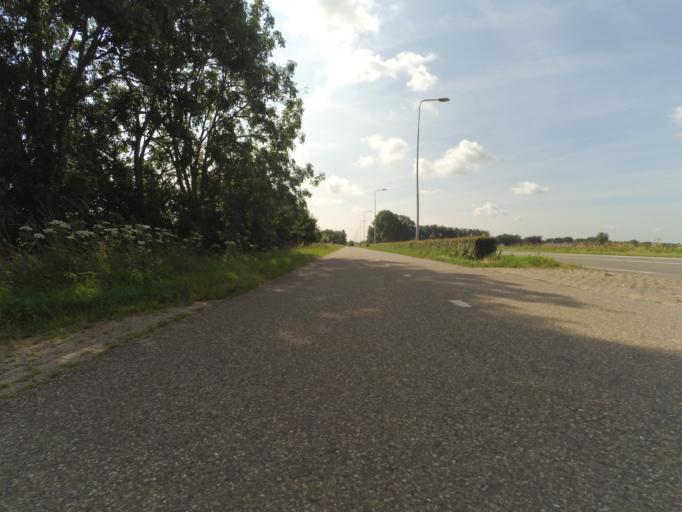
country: NL
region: Utrecht
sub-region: Gemeente Bunnik
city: Bunnik
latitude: 52.0421
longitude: 5.2317
